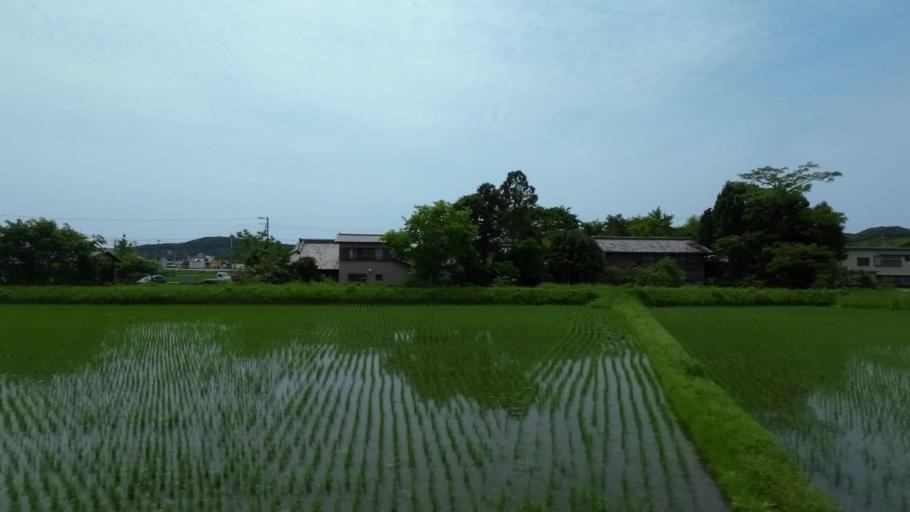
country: JP
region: Kochi
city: Kochi-shi
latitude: 33.5784
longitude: 133.6232
